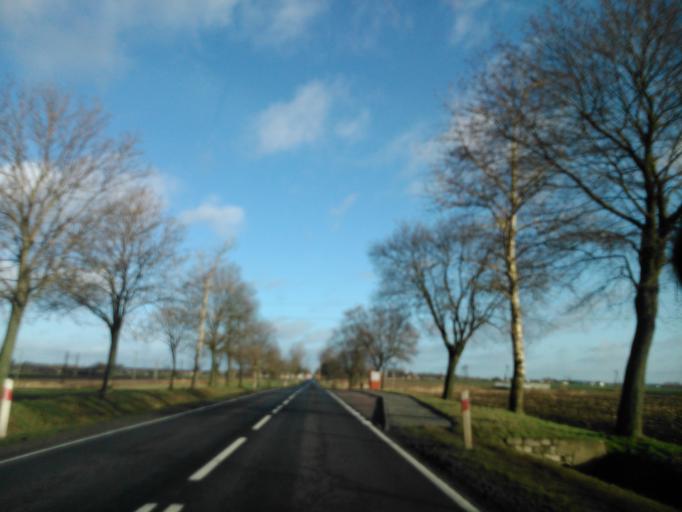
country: PL
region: Kujawsko-Pomorskie
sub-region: Powiat inowroclawski
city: Gniewkowo
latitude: 52.8804
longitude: 18.3841
